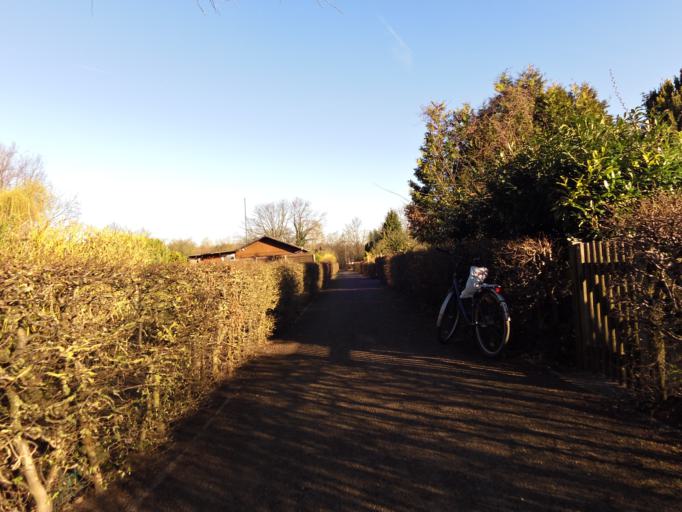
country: DE
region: Lower Saxony
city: Hannover
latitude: 52.3791
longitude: 9.7931
